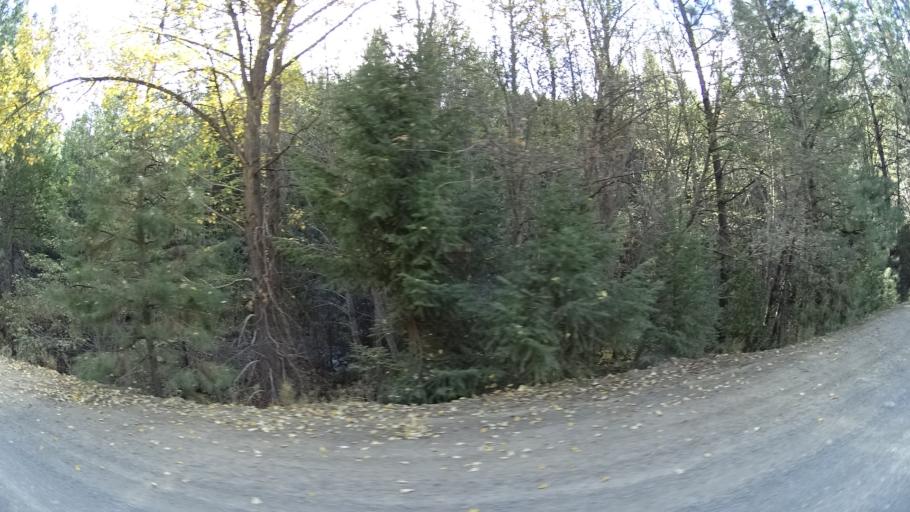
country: US
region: California
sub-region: Siskiyou County
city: Yreka
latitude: 41.7157
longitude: -122.7939
